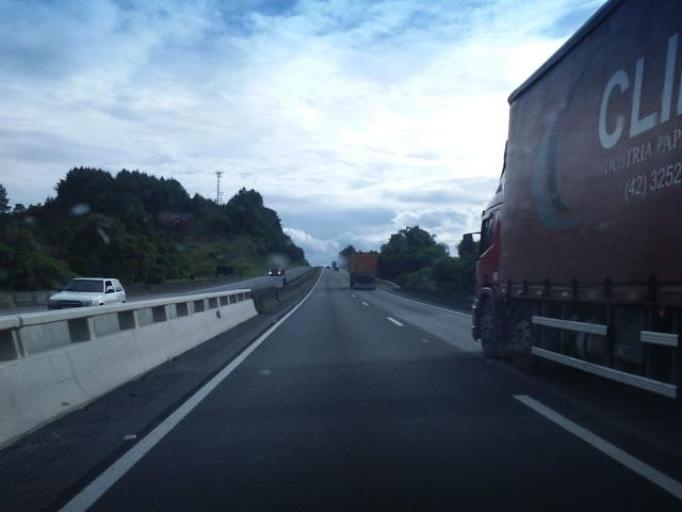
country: BR
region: Parana
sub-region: Campina Grande Do Sul
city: Campina Grande do Sul
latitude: -25.3333
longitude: -49.0334
